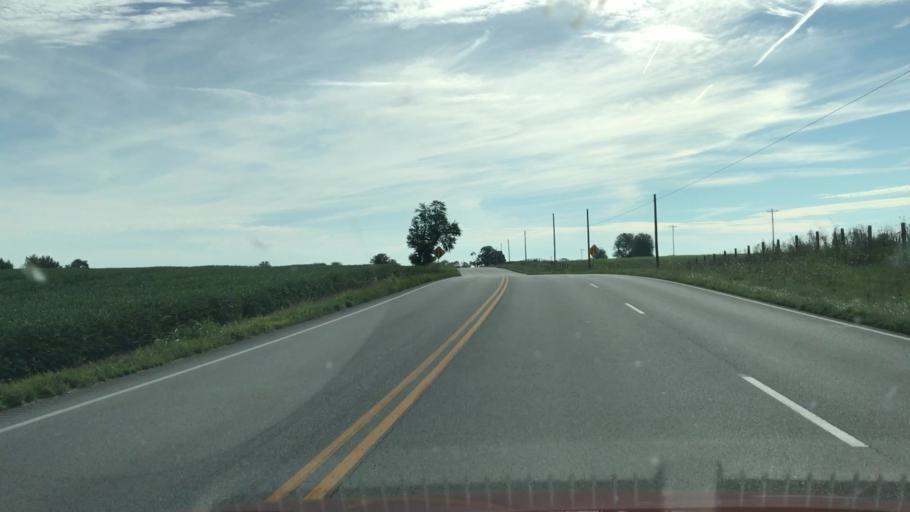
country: US
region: Kentucky
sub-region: Edmonson County
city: Brownsville
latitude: 37.0736
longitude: -86.2596
